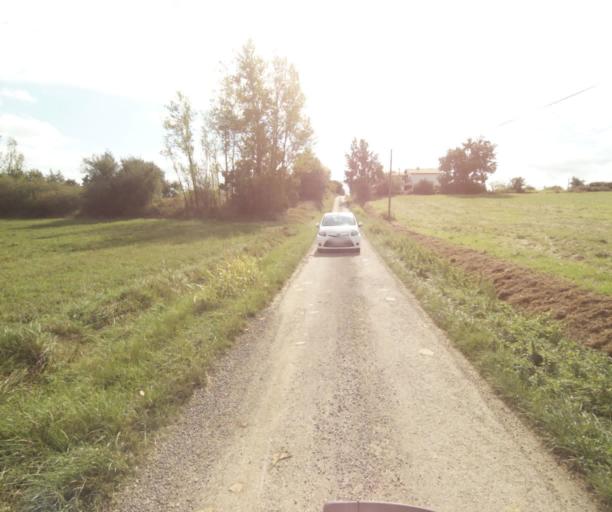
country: FR
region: Midi-Pyrenees
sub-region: Departement du Tarn-et-Garonne
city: Verdun-sur-Garonne
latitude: 43.8638
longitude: 1.1803
